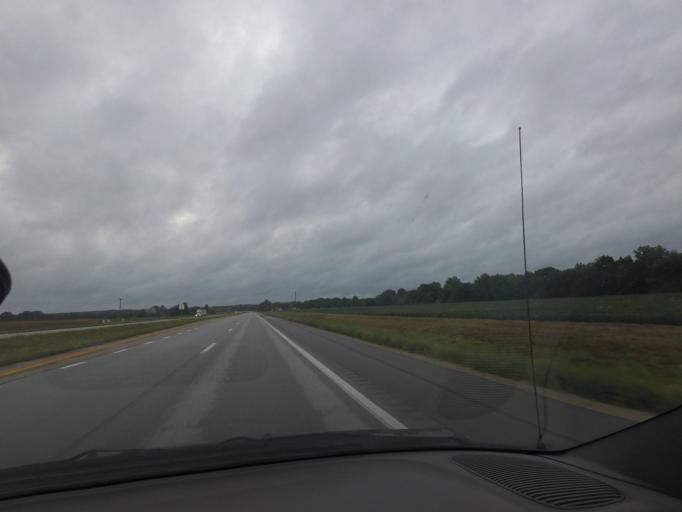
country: US
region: Missouri
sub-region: Shelby County
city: Shelbina
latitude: 39.6667
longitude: -91.9190
